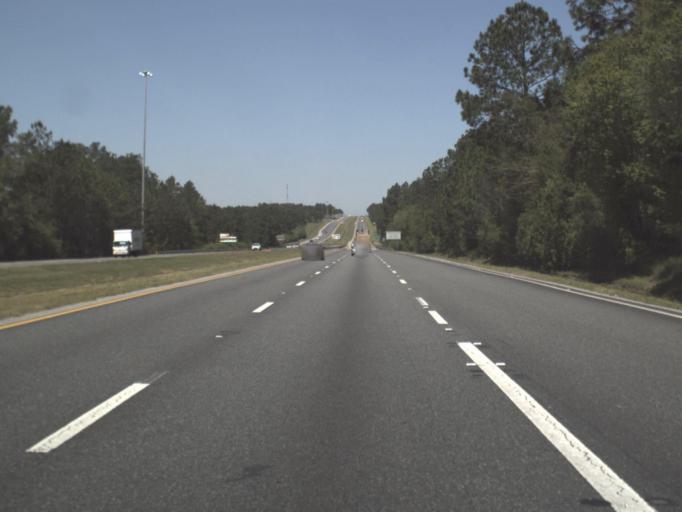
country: US
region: Florida
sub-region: Escambia County
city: Gonzalez
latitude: 30.5361
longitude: -87.3364
